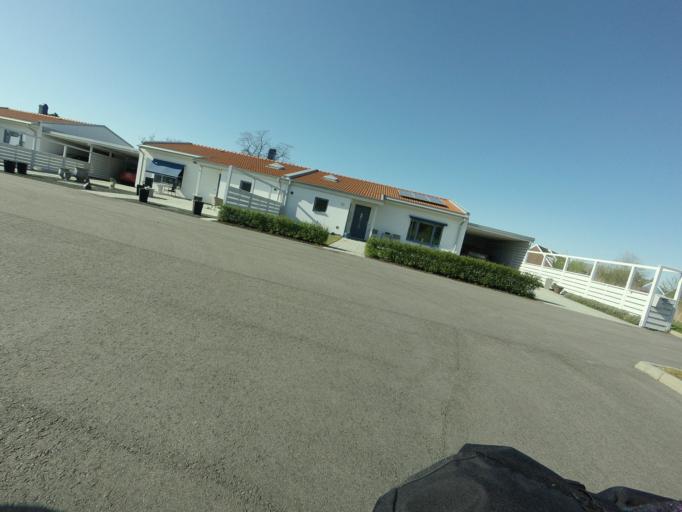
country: SE
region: Skane
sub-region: Landskrona
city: Asmundtorp
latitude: 55.8465
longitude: 12.9266
